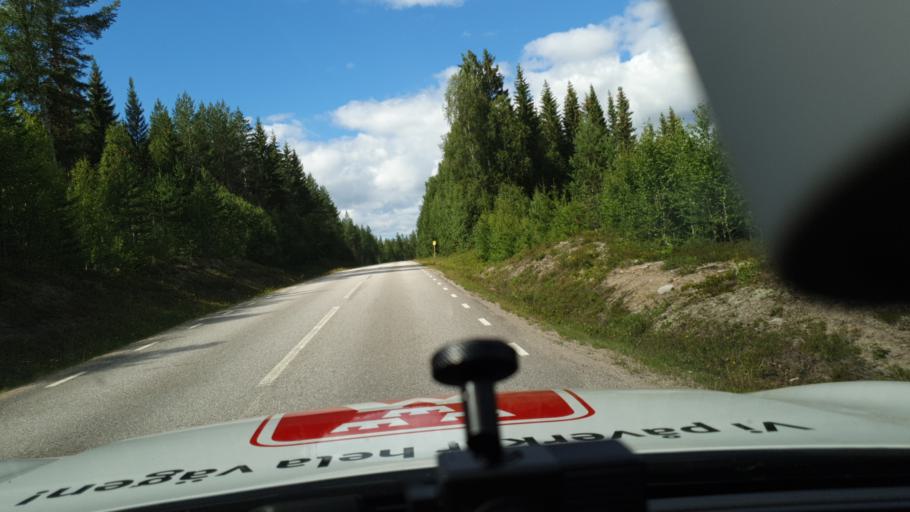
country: NO
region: Hedmark
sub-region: Trysil
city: Innbygda
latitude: 61.0213
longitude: 12.4693
